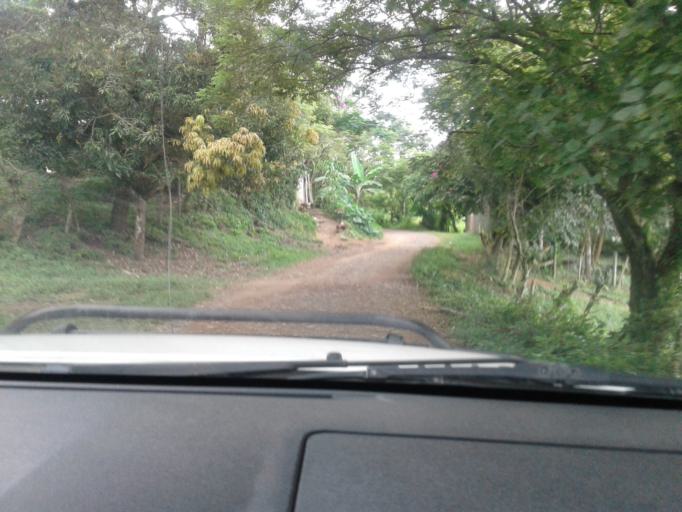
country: NI
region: Matagalpa
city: San Ramon
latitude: 12.9049
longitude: -85.7407
